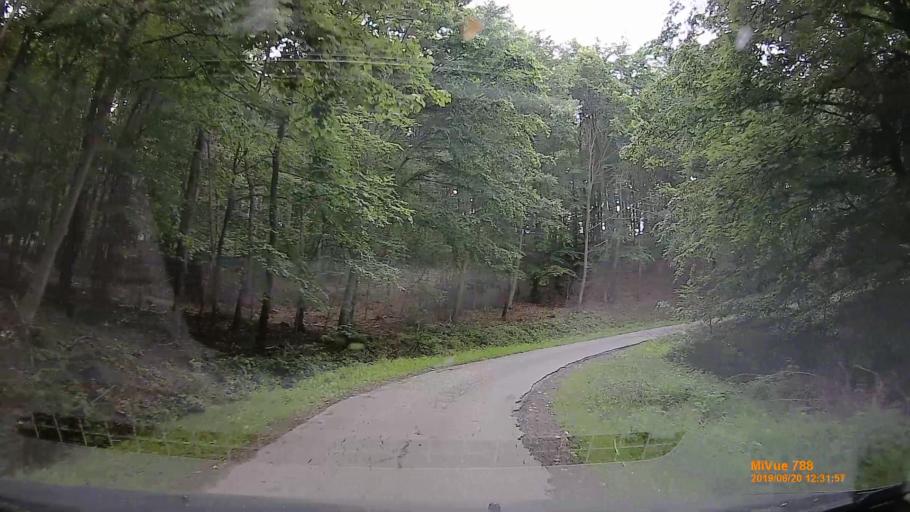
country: HU
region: Baranya
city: Hosszuheteny
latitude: 46.1964
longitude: 18.3620
